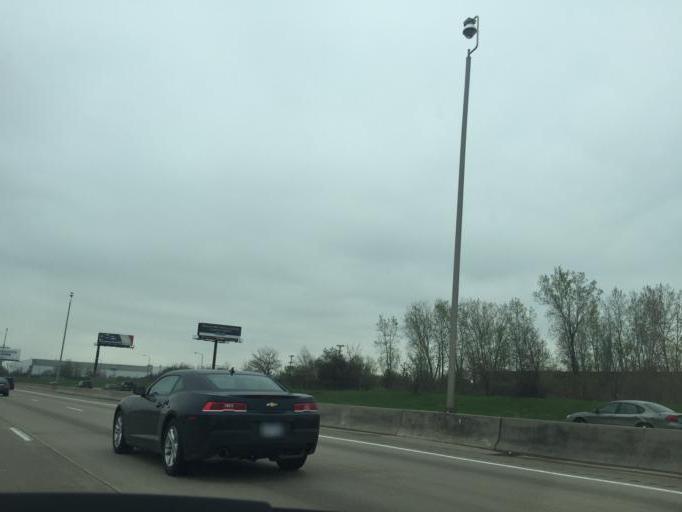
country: US
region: Michigan
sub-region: Wayne County
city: Dearborn
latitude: 42.3792
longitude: -83.1951
